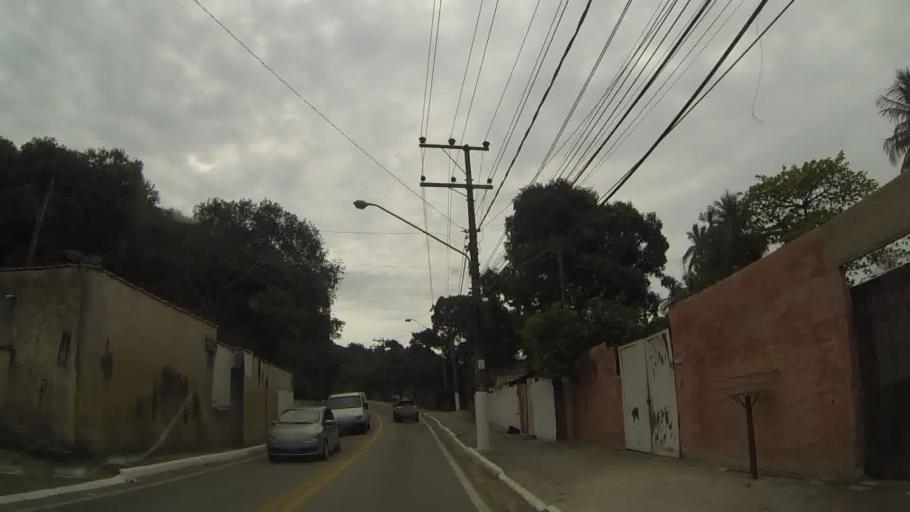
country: BR
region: Sao Paulo
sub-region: Sao Sebastiao
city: Sao Sebastiao
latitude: -23.8127
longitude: -45.4092
